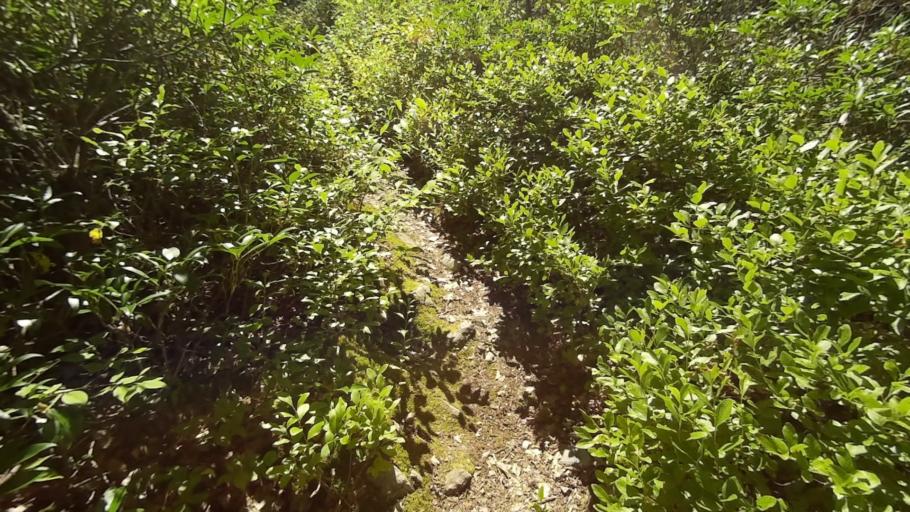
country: US
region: Pennsylvania
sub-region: Centre County
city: Boalsburg
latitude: 40.7195
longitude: -77.7800
